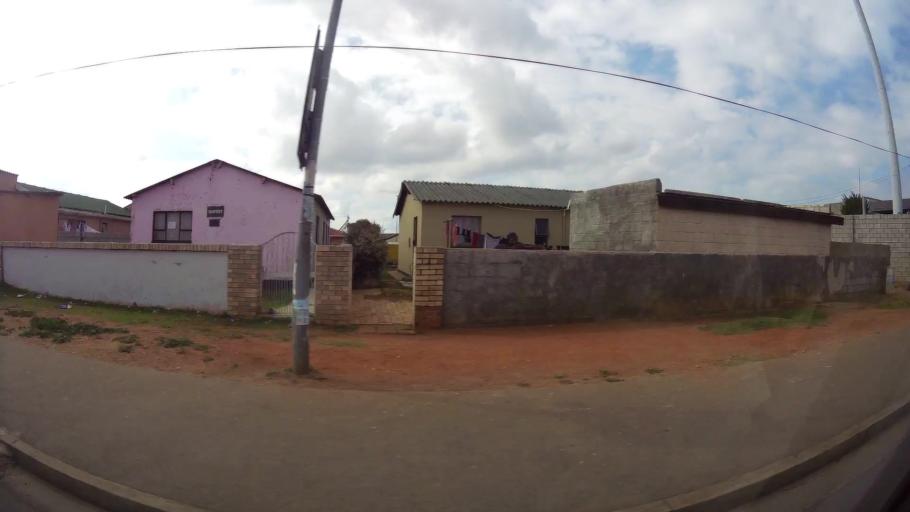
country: ZA
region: Eastern Cape
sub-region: Nelson Mandela Bay Metropolitan Municipality
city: Port Elizabeth
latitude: -33.8185
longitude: 25.5853
